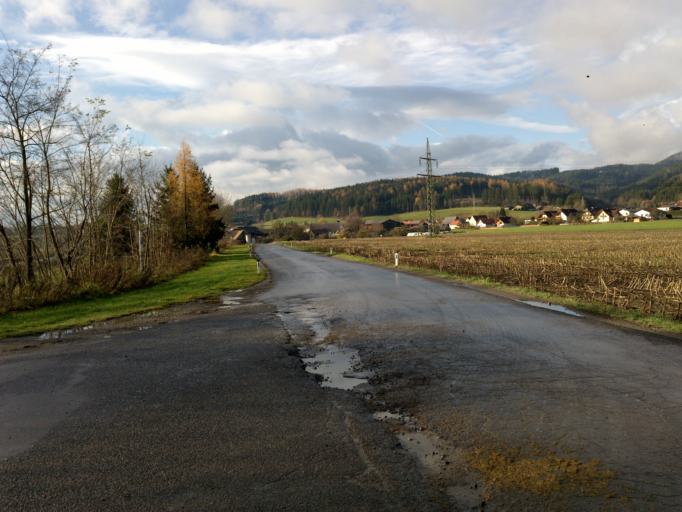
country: AT
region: Styria
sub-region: Politischer Bezirk Murtal
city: Kobenz
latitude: 47.2391
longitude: 14.8415
